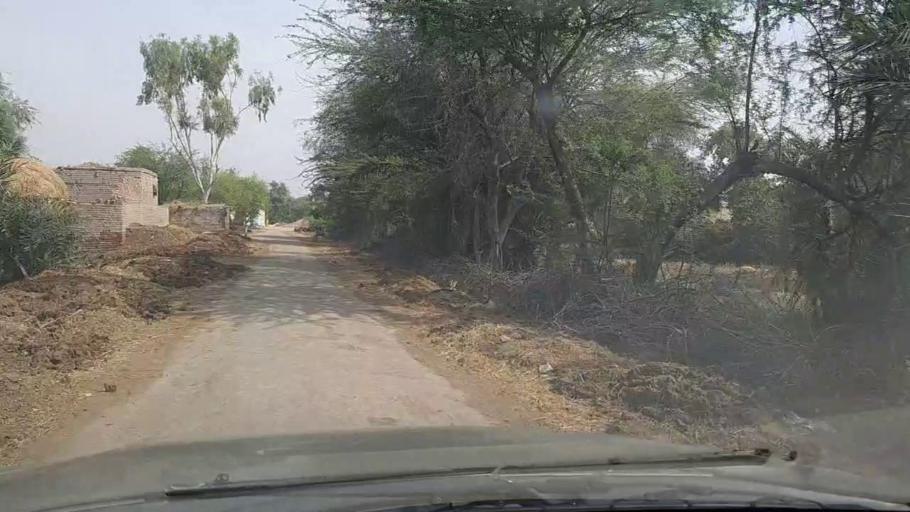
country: PK
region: Sindh
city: Lakhi
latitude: 27.8421
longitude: 68.7610
